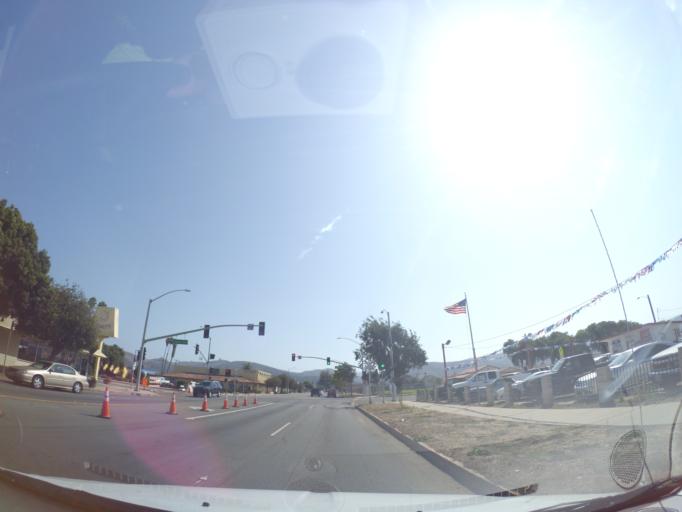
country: US
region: California
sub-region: Santa Barbara County
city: Lompoc
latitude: 34.6443
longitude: -120.4580
